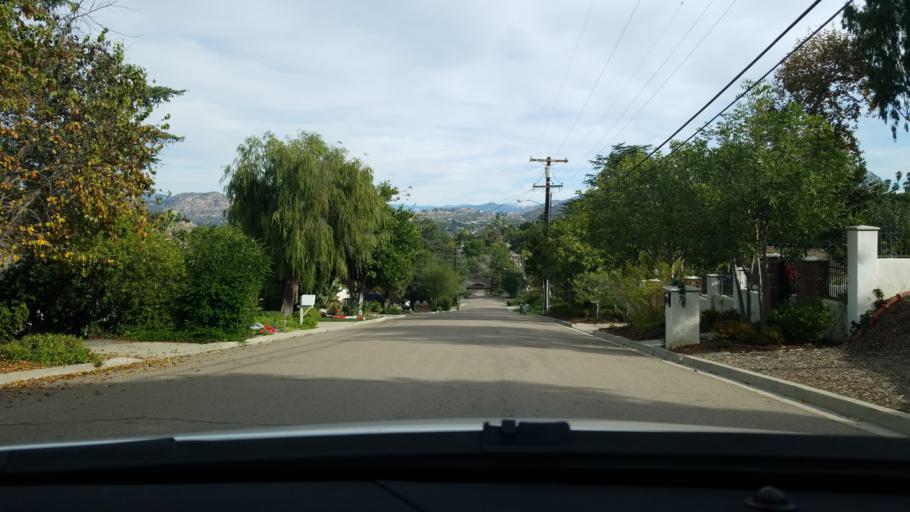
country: US
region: California
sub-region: San Diego County
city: Casa de Oro-Mount Helix
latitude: 32.7716
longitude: -116.9474
